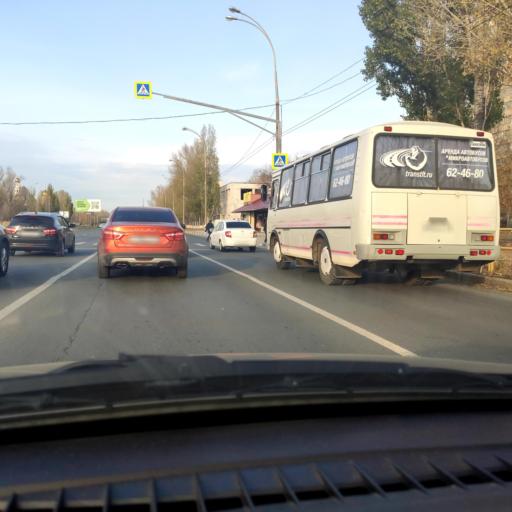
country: RU
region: Samara
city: Tol'yatti
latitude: 53.5245
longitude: 49.2807
